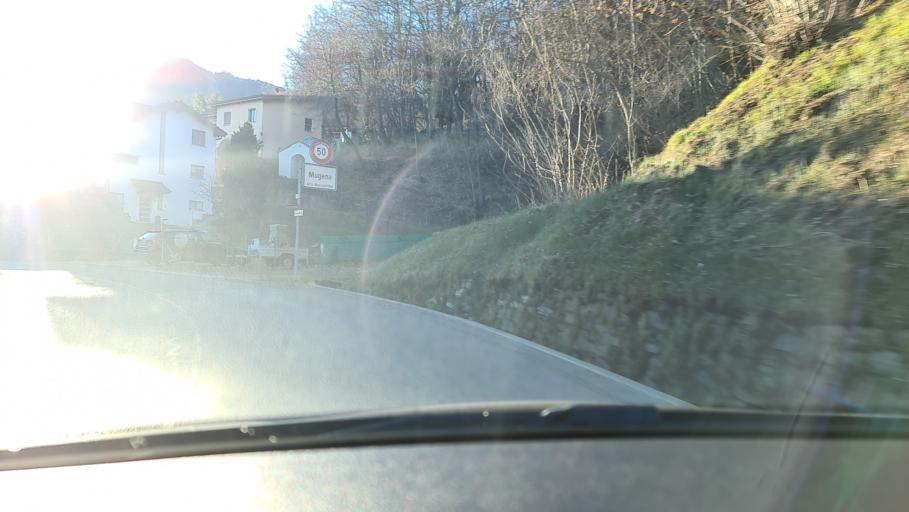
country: CH
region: Ticino
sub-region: Lugano District
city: Gravesano
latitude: 46.0477
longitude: 8.8946
